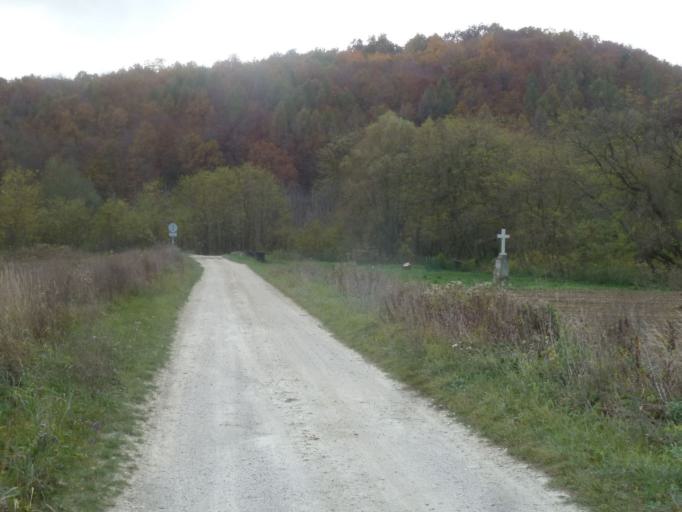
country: HU
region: Zala
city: Pacsa
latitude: 46.6060
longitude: 17.0657
